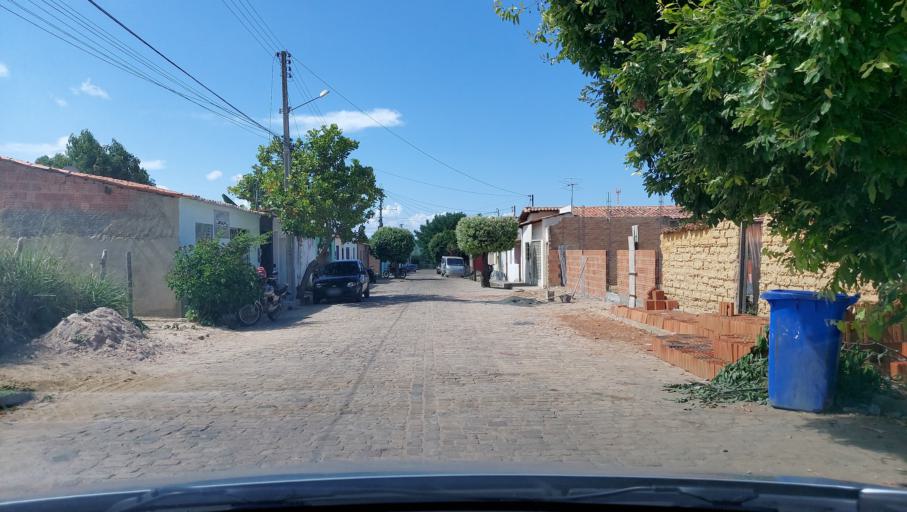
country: BR
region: Bahia
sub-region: Oliveira Dos Brejinhos
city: Beira Rio
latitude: -11.9989
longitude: -42.6301
